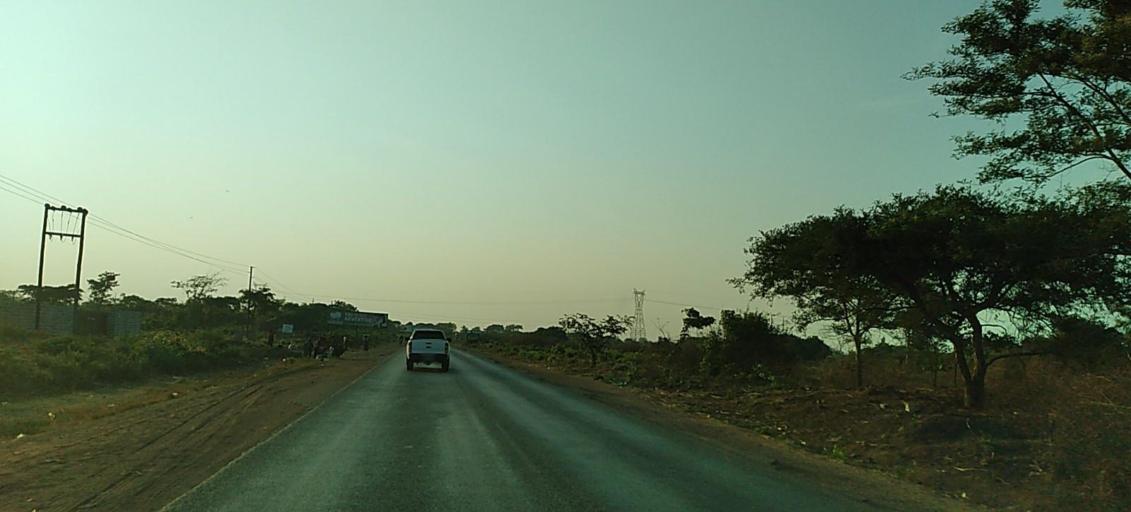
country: ZM
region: Copperbelt
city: Ndola
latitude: -13.0420
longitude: 28.6952
